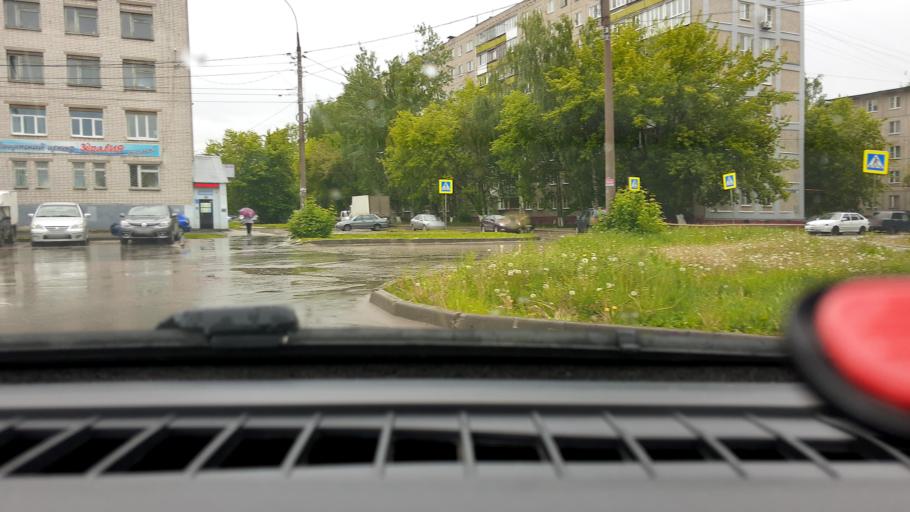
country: RU
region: Nizjnij Novgorod
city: Gorbatovka
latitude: 56.2626
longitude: 43.8754
